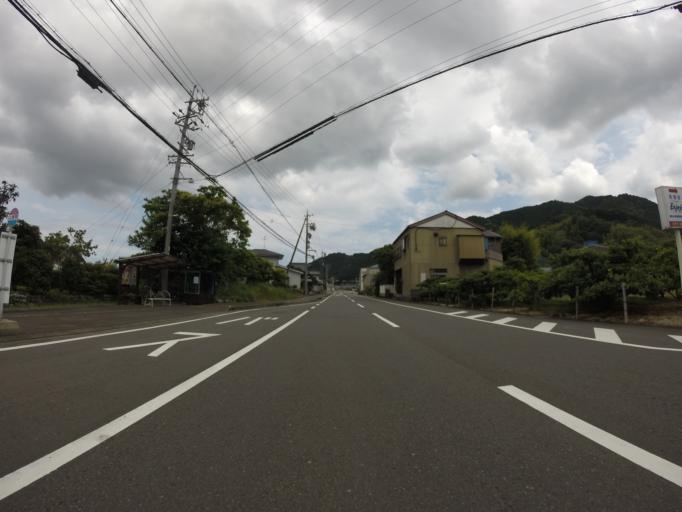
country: JP
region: Shizuoka
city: Shizuoka-shi
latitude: 34.9822
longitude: 138.3065
